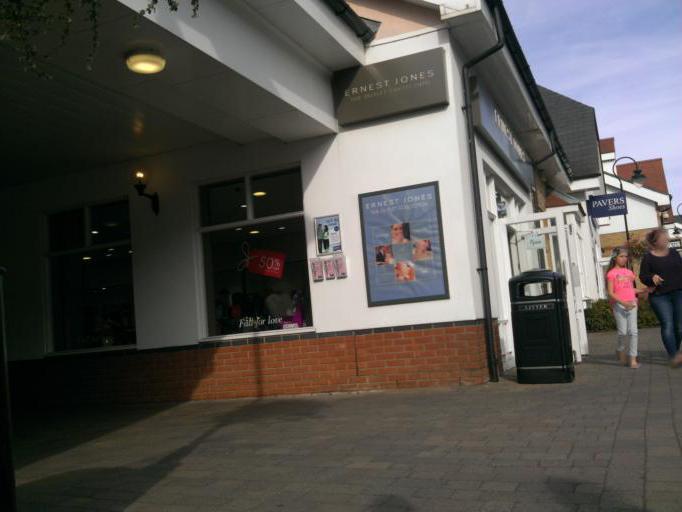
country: GB
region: England
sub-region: Essex
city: Rayne
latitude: 51.8705
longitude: 0.5706
